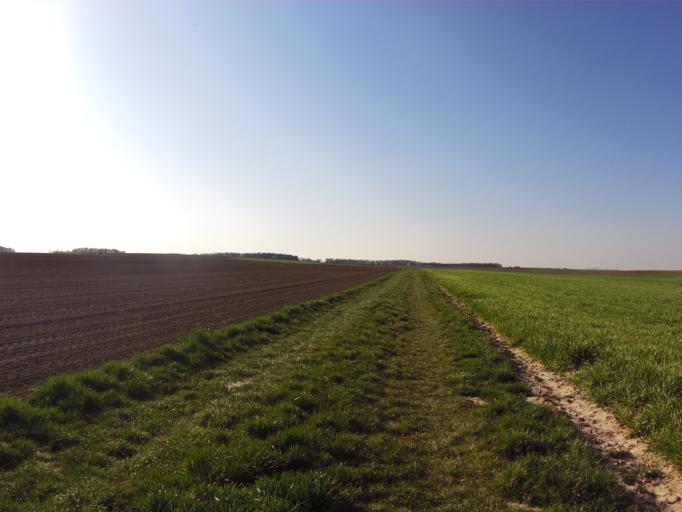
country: DE
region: Bavaria
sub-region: Regierungsbezirk Unterfranken
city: Oberpleichfeld
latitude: 49.8366
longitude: 10.0879
